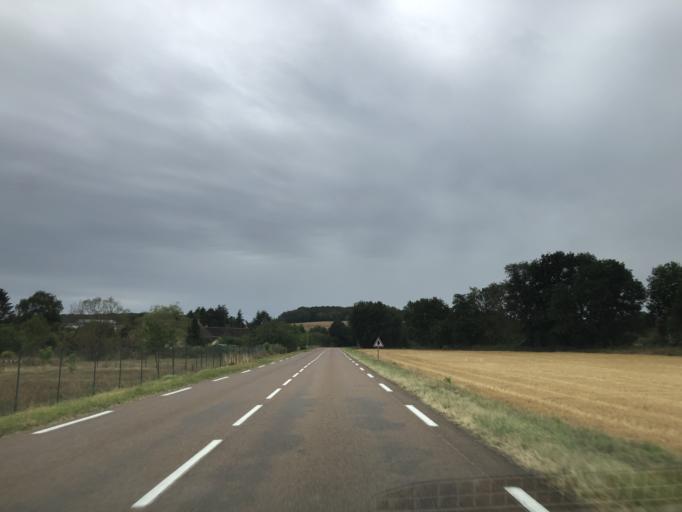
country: FR
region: Bourgogne
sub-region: Departement de l'Yonne
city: Saint-Julien-du-Sault
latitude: 47.9328
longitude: 3.2425
